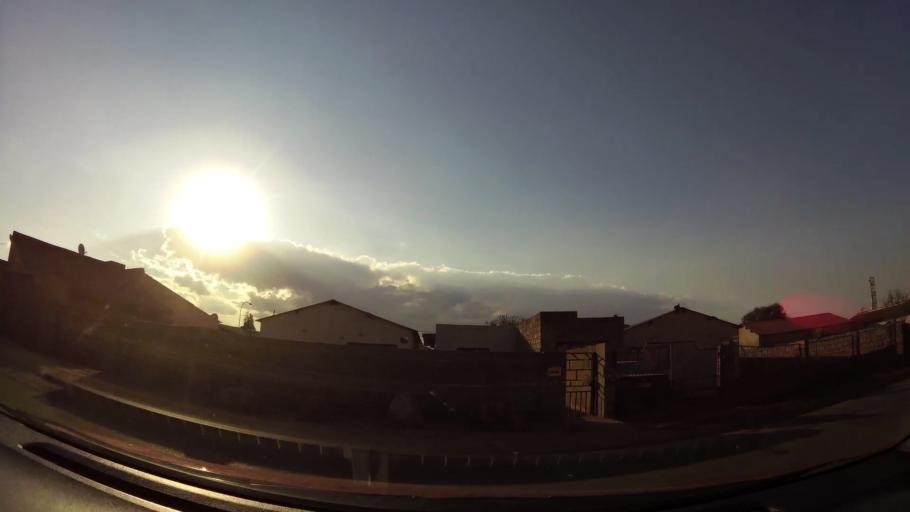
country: ZA
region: Gauteng
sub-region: City of Johannesburg Metropolitan Municipality
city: Soweto
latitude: -26.2278
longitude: 27.8541
